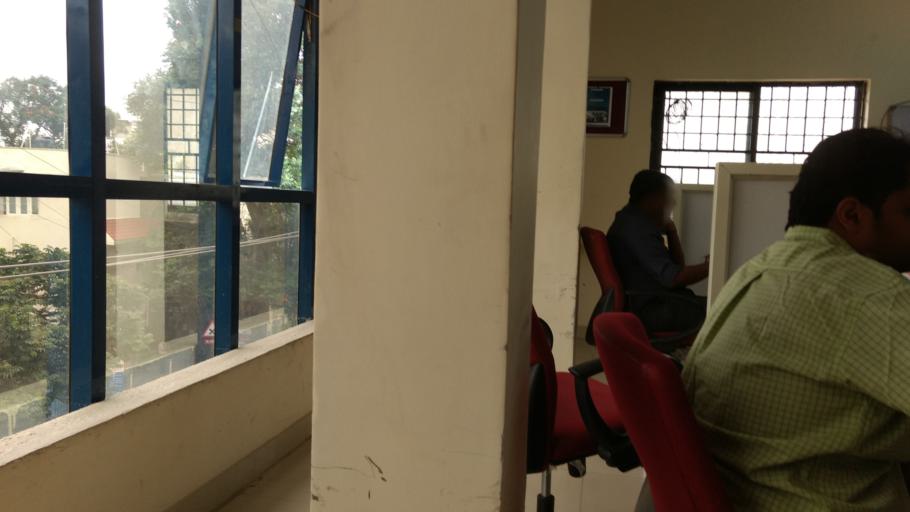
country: IN
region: Karnataka
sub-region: Bangalore Urban
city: Bangalore
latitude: 13.0220
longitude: 77.6391
